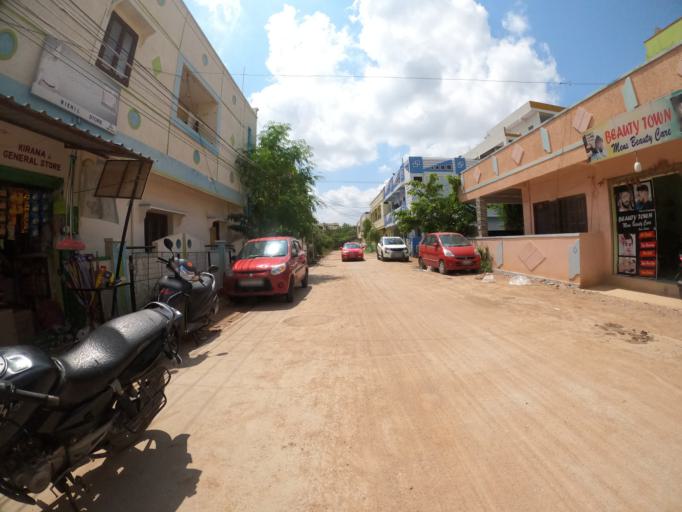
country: IN
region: Telangana
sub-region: Hyderabad
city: Hyderabad
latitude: 17.3628
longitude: 78.3833
